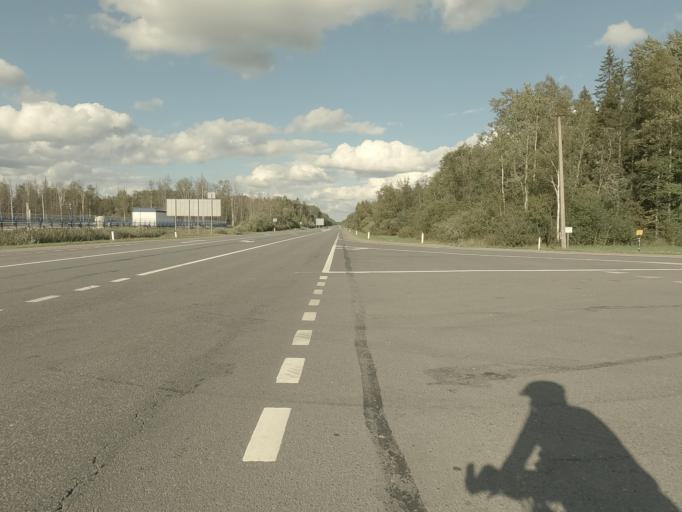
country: RU
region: Leningrad
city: Ul'yanovka
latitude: 59.6457
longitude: 30.8412
